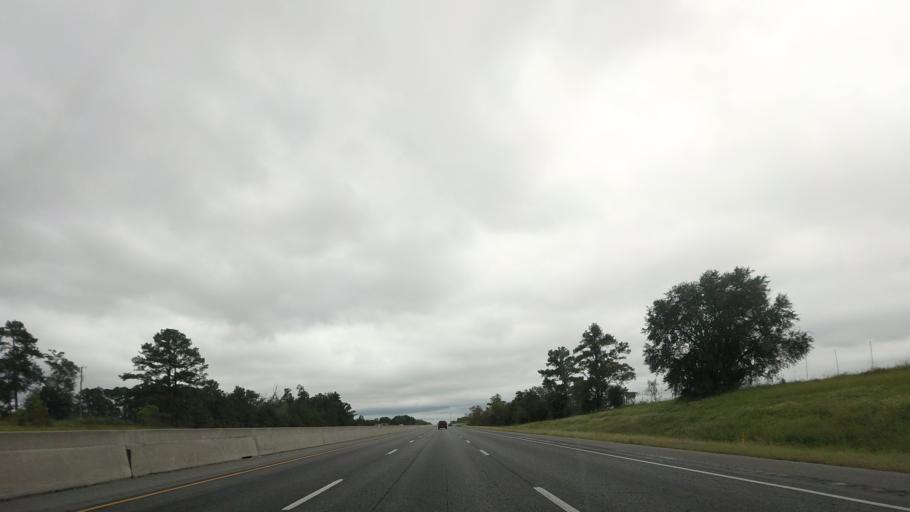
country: US
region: Georgia
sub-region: Lowndes County
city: Hahira
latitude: 30.9646
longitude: -83.3797
